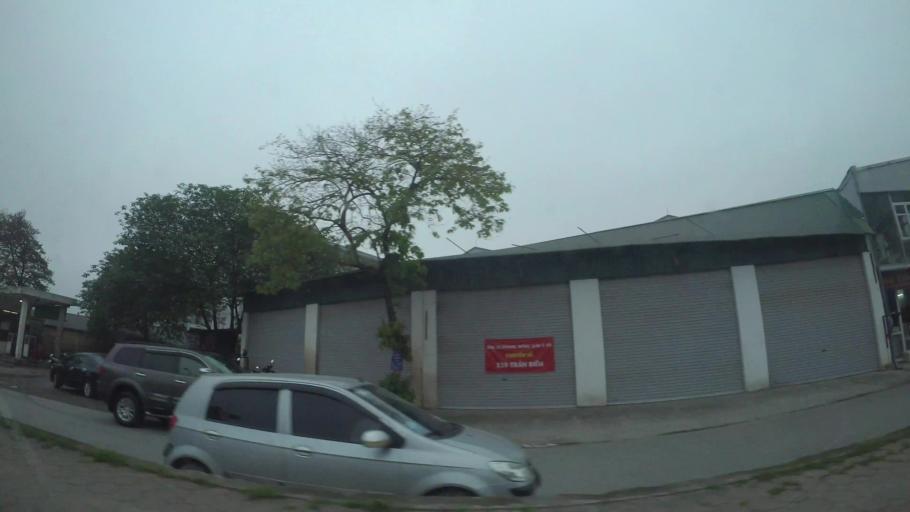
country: VN
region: Ha Noi
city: Hai BaTrung
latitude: 20.9983
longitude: 105.8359
